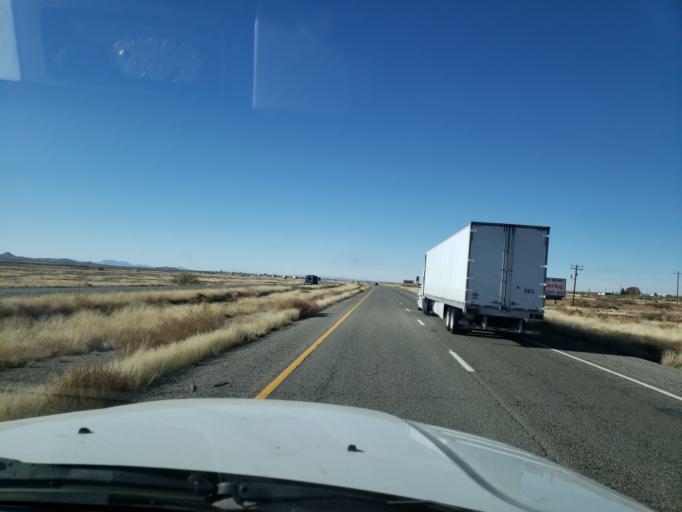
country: US
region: New Mexico
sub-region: Hidalgo County
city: Lordsburg
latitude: 32.3264
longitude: -108.6309
